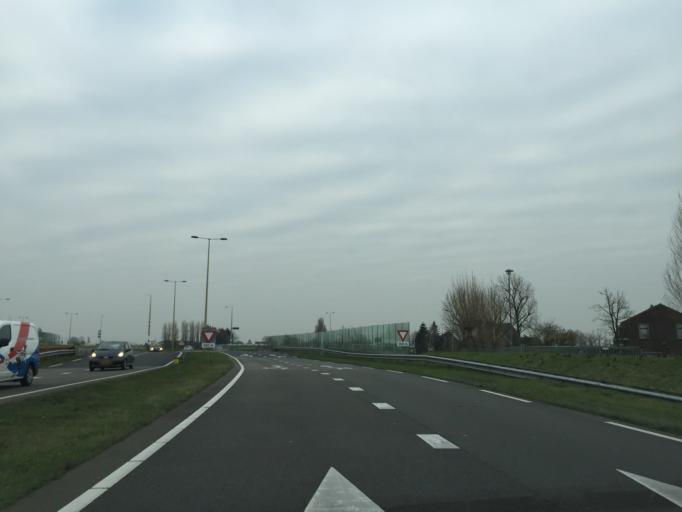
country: NL
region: South Holland
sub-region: Gemeente Pijnacker-Nootdorp
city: Pijnacker
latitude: 52.0005
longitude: 4.4376
